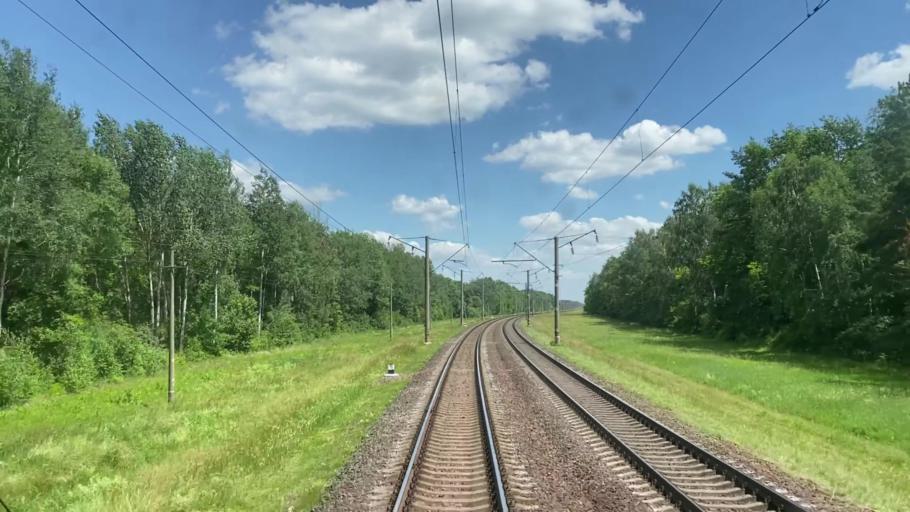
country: BY
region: Brest
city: Pruzhany
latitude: 52.5007
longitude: 24.6202
